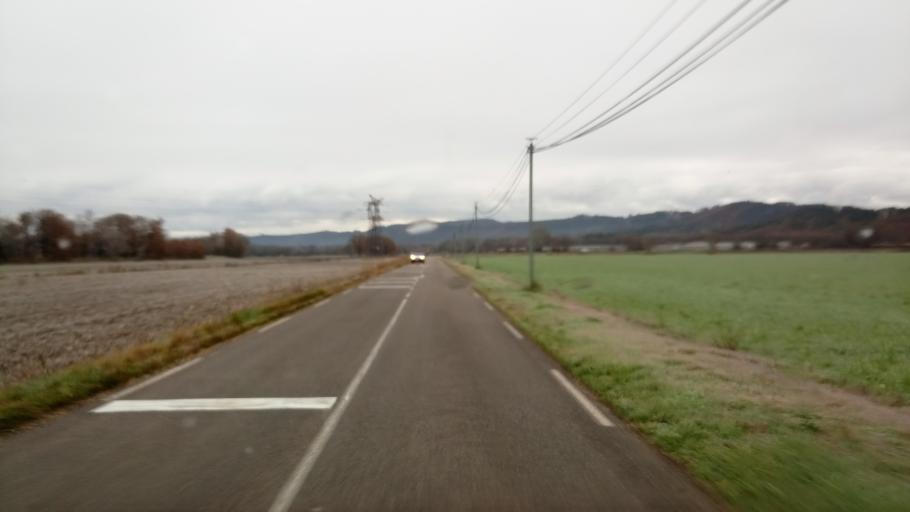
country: FR
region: Provence-Alpes-Cote d'Azur
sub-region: Departement du Var
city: Vinon-sur-Verdon
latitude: 43.7283
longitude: 5.8309
